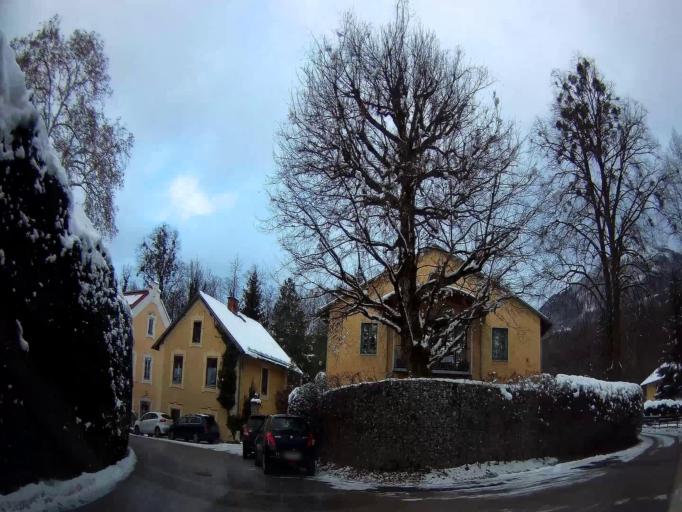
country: AT
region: Salzburg
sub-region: Politischer Bezirk Salzburg-Umgebung
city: Elsbethen
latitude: 47.7859
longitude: 13.0895
